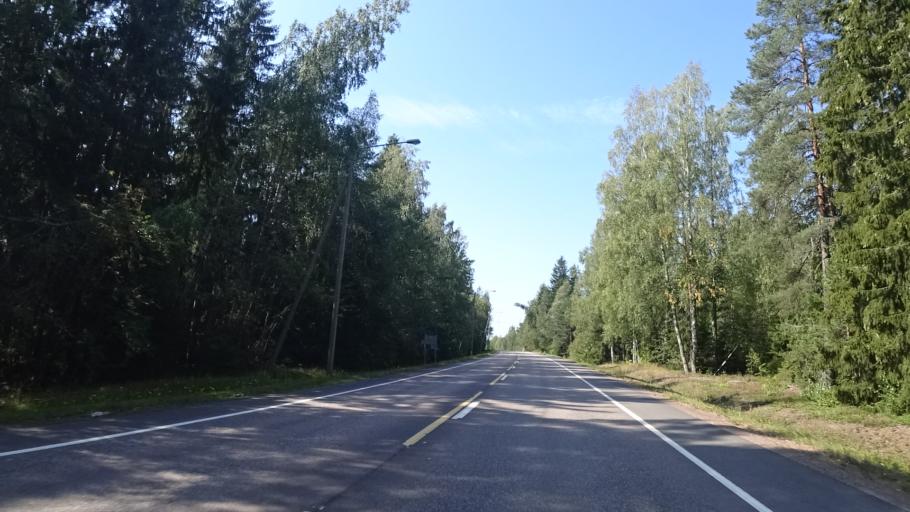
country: FI
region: Kymenlaakso
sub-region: Kotka-Hamina
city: Karhula
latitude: 60.5612
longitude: 27.0333
